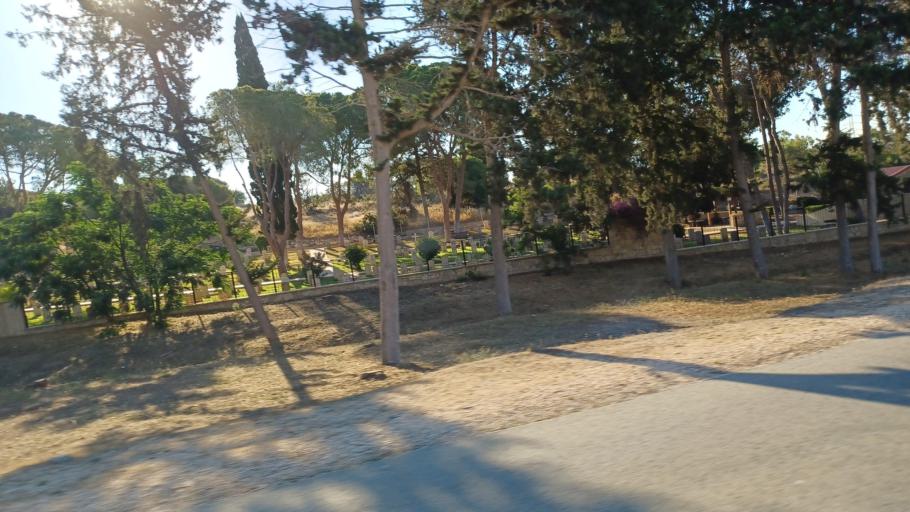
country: CY
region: Larnaka
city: Xylotymbou
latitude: 34.9905
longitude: 33.7422
